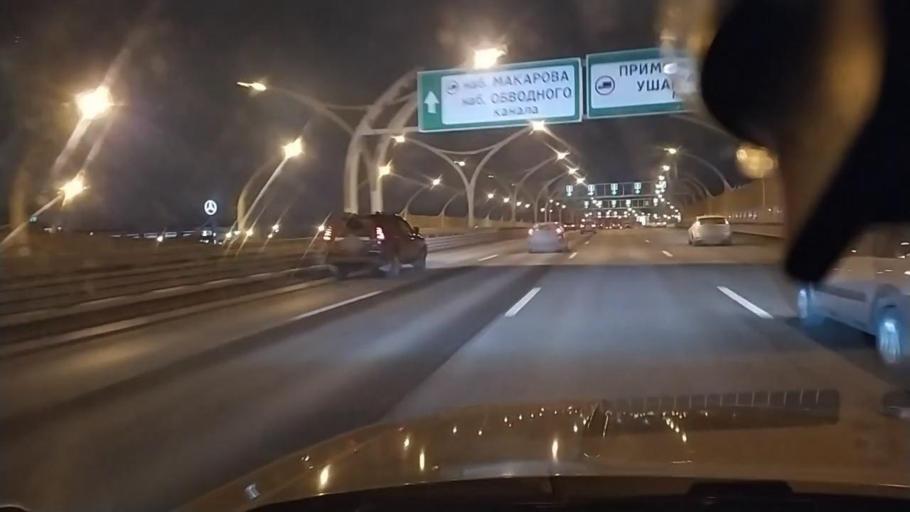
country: RU
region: St.-Petersburg
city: Staraya Derevnya
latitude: 59.9868
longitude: 30.2301
